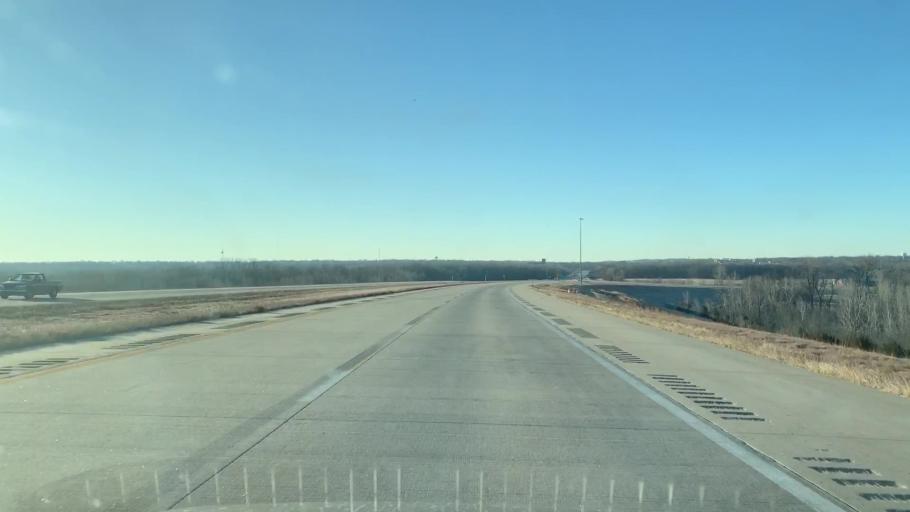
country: US
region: Kansas
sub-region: Bourbon County
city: Fort Scott
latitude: 37.8613
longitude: -94.7030
